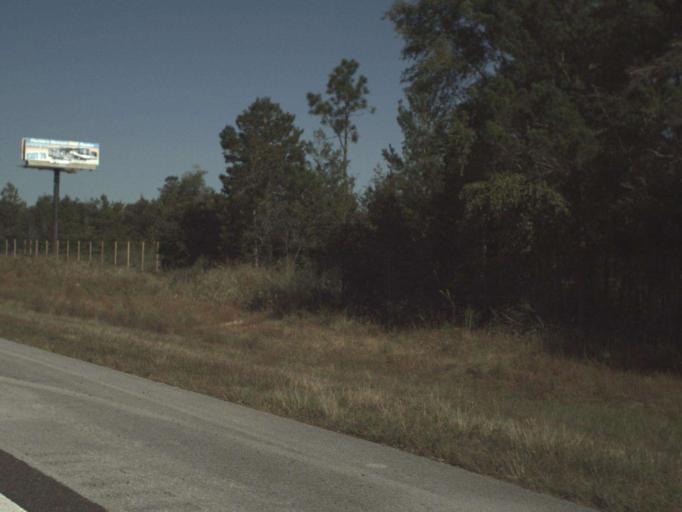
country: US
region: Florida
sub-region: Walton County
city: DeFuniak Springs
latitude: 30.7440
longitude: -86.2312
